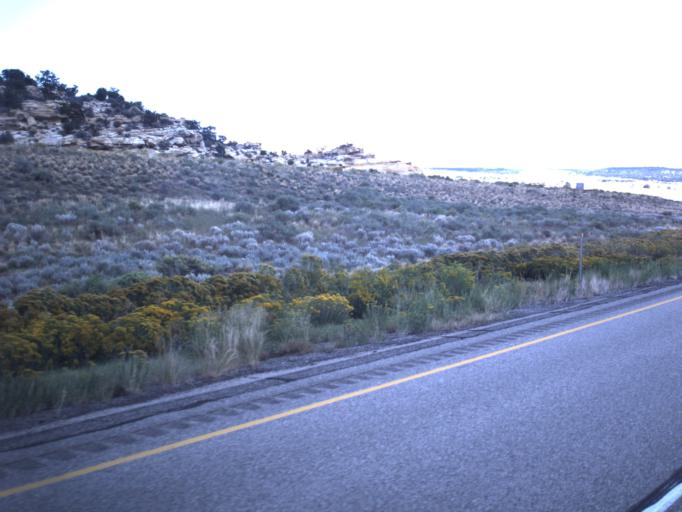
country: US
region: Utah
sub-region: Emery County
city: Ferron
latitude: 38.8645
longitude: -110.7966
